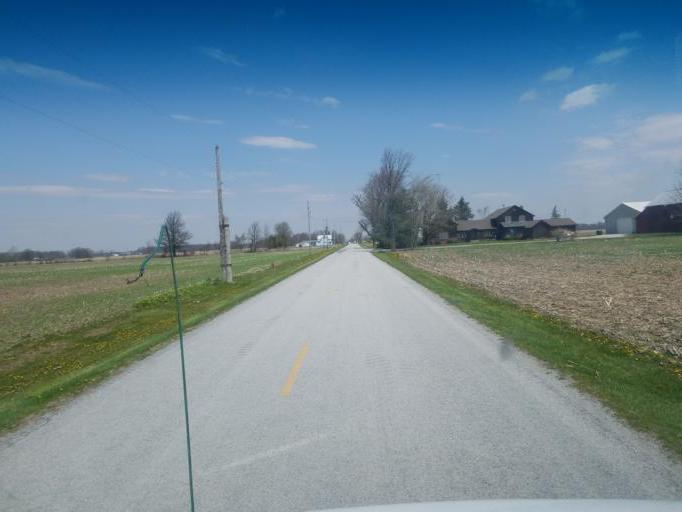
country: US
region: Ohio
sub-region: Hardin County
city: Forest
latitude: 40.7343
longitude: -83.5378
